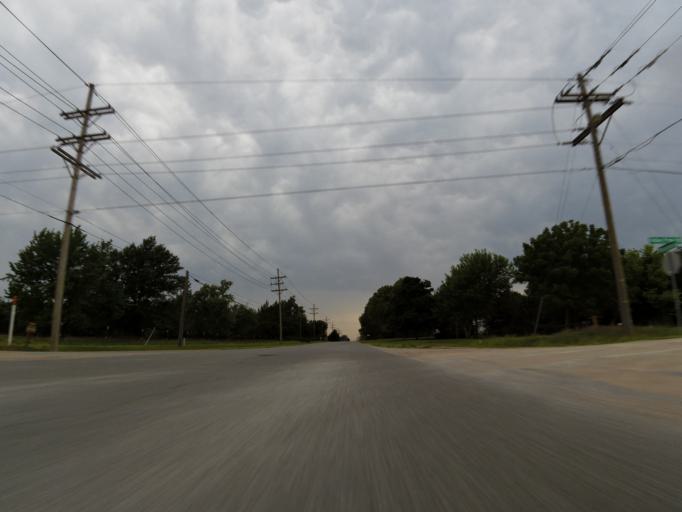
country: US
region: Kansas
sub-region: Reno County
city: South Hutchinson
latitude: 38.0281
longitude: -97.9585
